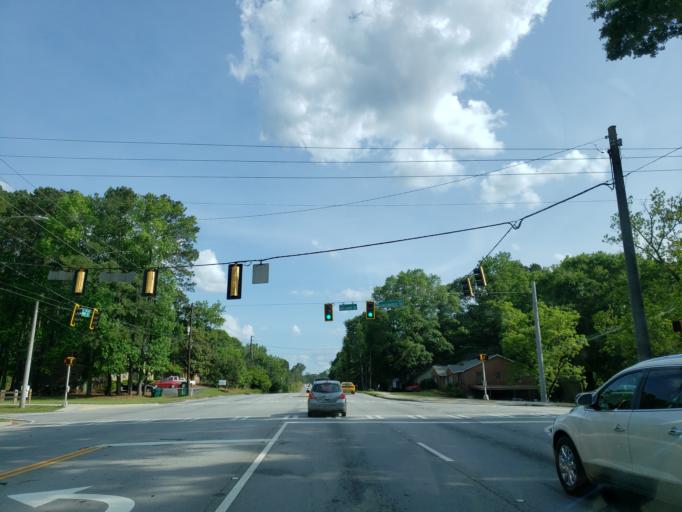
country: US
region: Georgia
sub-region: Carroll County
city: Carrollton
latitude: 33.5917
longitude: -85.0793
